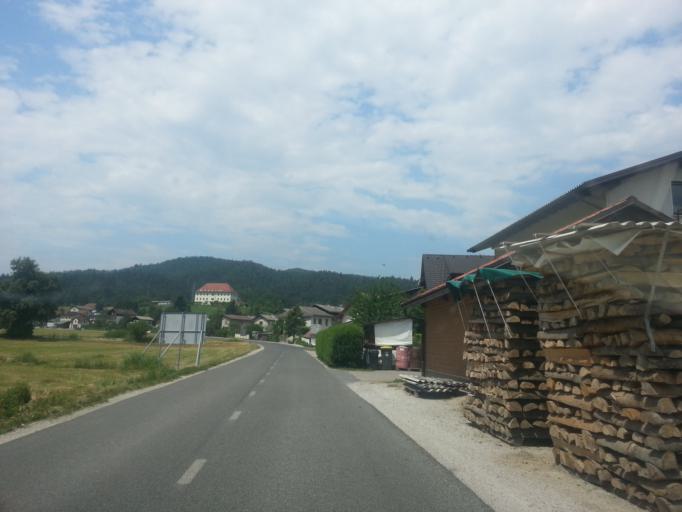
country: SI
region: Brezovica
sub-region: Opstina Ljubljana-Vic-Rudnik
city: Brezovica pri Ljubljani
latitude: 46.0530
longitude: 14.4176
